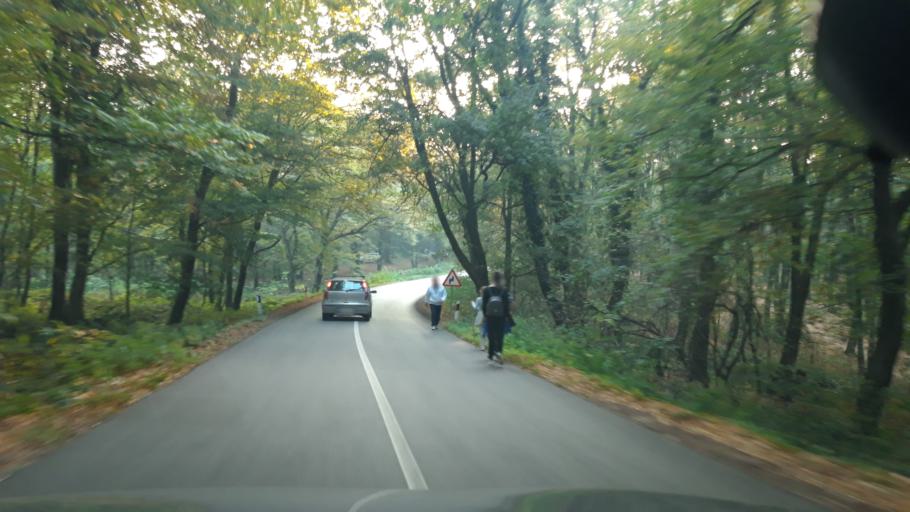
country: RS
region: Autonomna Pokrajina Vojvodina
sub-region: Sremski Okrug
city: Irig
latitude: 45.1551
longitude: 19.8546
